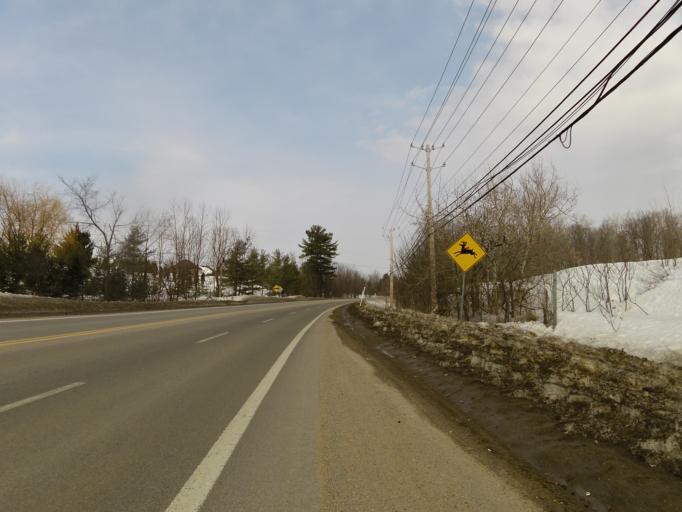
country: CA
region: Quebec
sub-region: Outaouais
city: Gatineau
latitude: 45.4850
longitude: -75.7558
